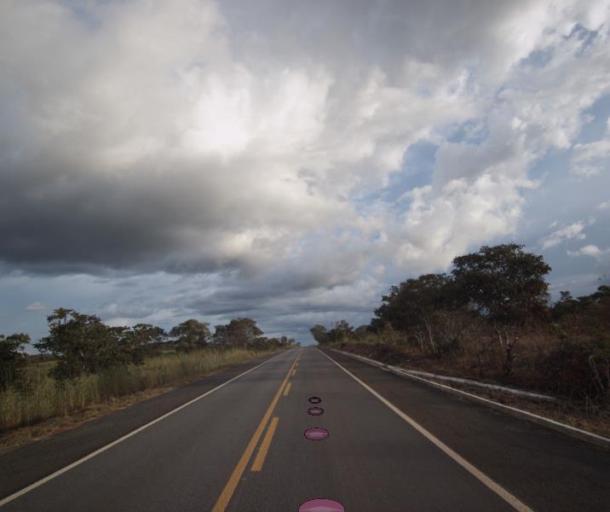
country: BR
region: Goias
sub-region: Barro Alto
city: Barro Alto
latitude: -14.8515
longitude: -48.6389
